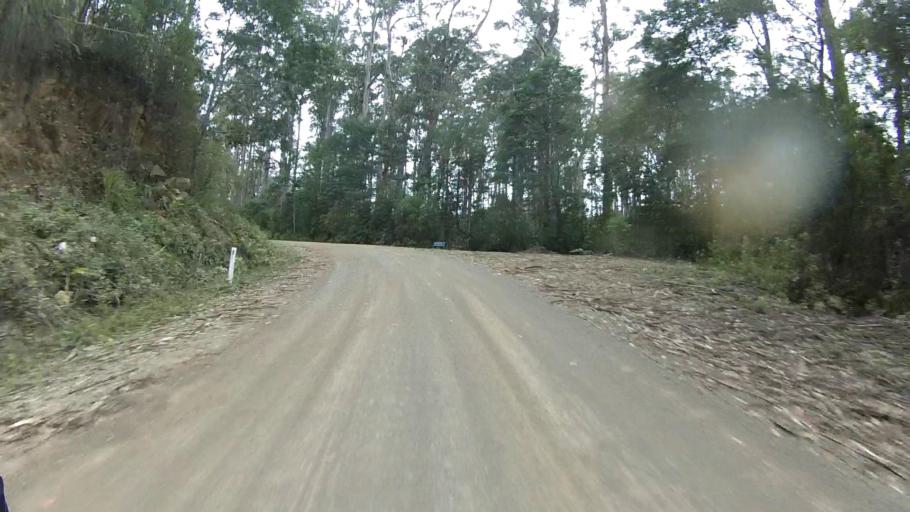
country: AU
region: Tasmania
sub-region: Sorell
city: Sorell
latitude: -42.7039
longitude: 147.8563
